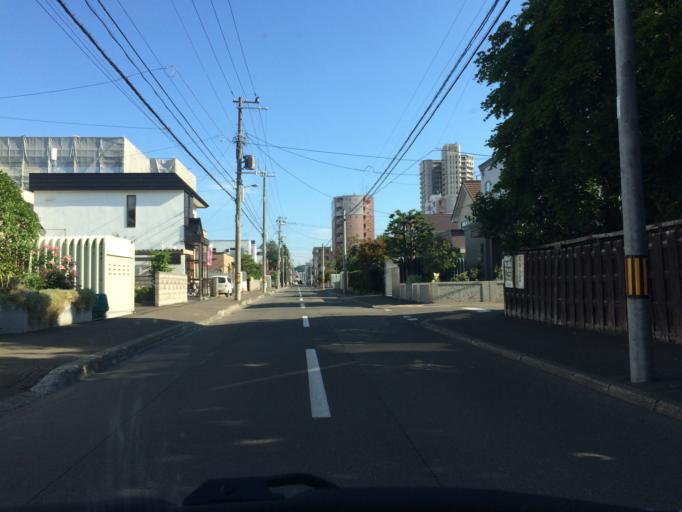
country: JP
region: Hokkaido
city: Sapporo
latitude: 43.0369
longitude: 141.3426
